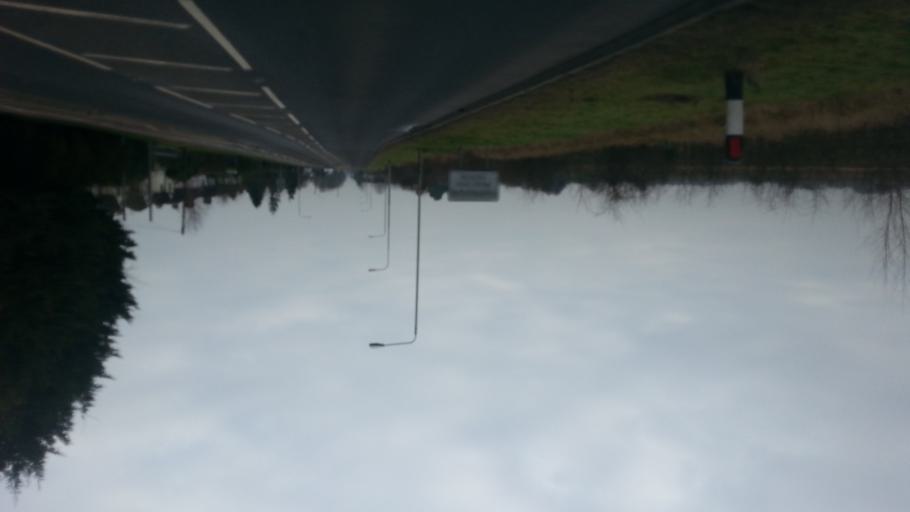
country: GB
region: England
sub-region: Nottinghamshire
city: Farndon
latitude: 53.0631
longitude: -0.8374
